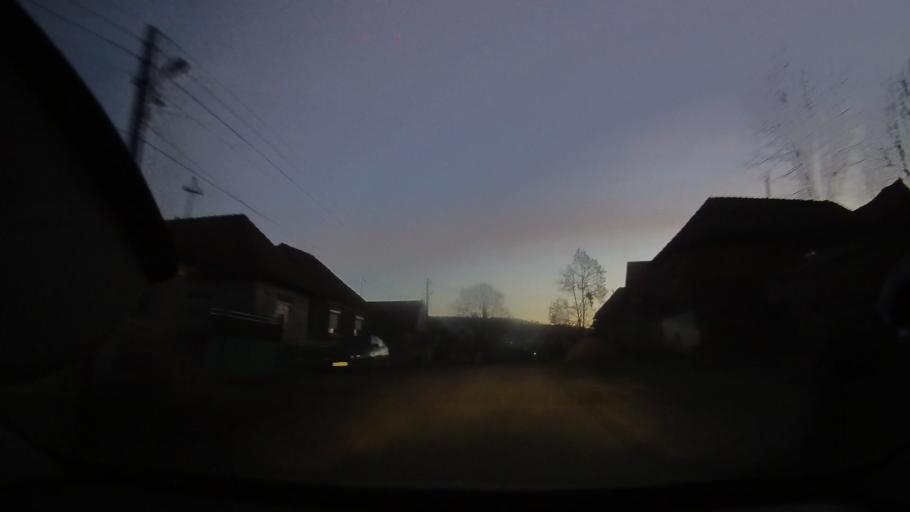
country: RO
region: Bihor
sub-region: Comuna Varciorog
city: Varciorog
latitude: 46.9831
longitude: 22.3275
